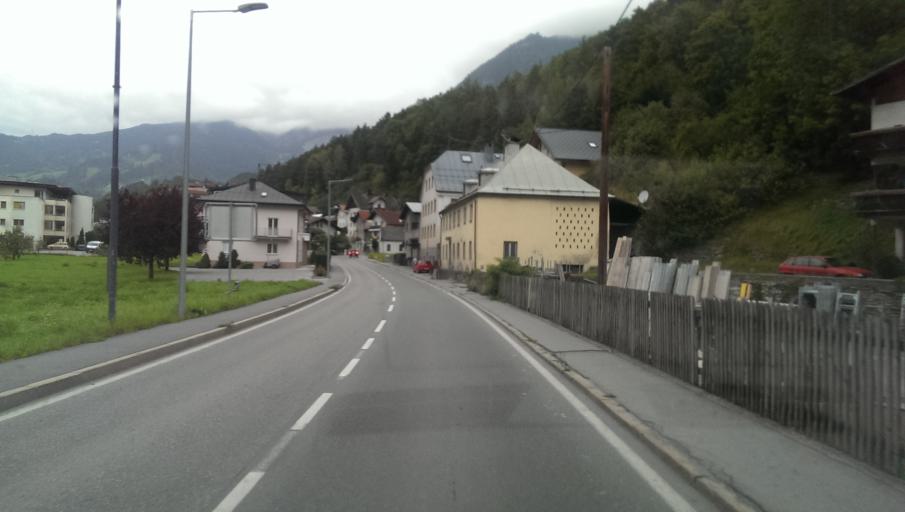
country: AT
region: Tyrol
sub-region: Politischer Bezirk Landeck
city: Stanz bei Landeck
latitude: 47.1411
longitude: 10.5531
